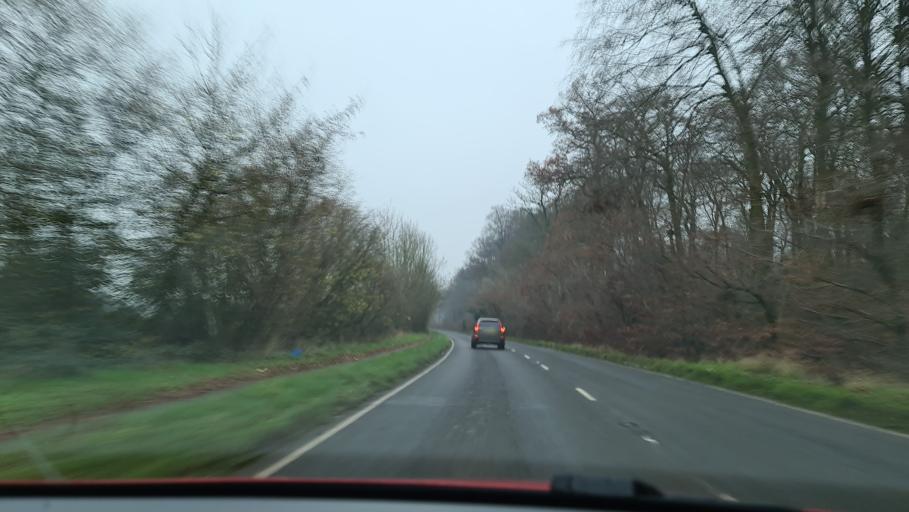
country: GB
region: England
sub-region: Buckinghamshire
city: Stokenchurch
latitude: 51.6539
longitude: -0.8759
